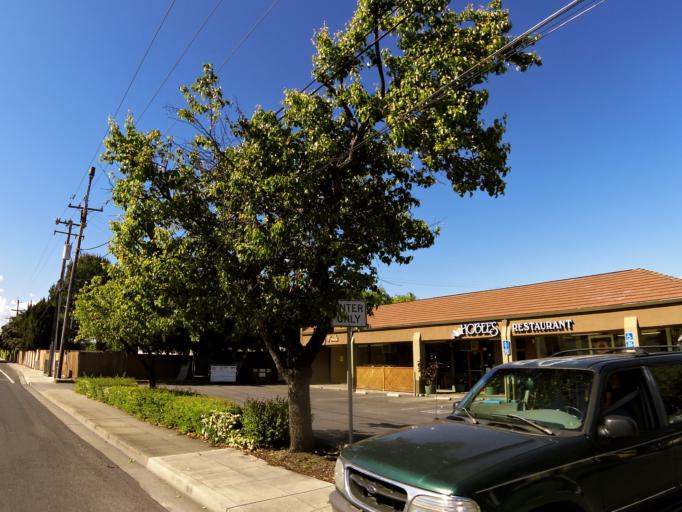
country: US
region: California
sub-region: Santa Clara County
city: Mountain View
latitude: 37.4036
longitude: -122.0981
